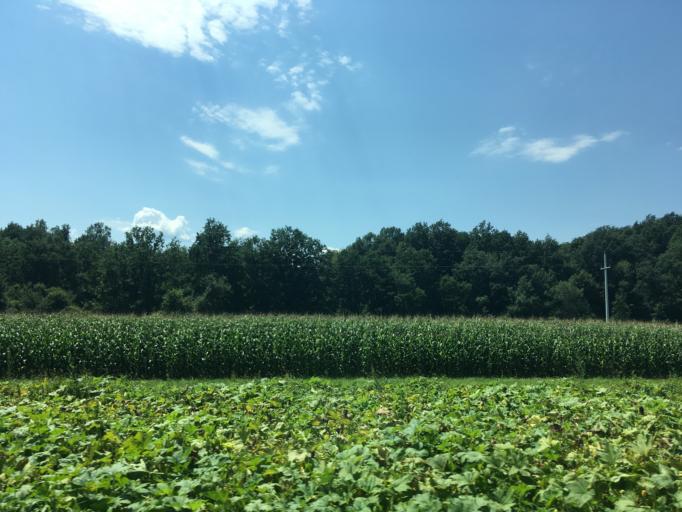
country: SI
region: Metlika
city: Metlika
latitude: 45.6118
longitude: 15.3274
